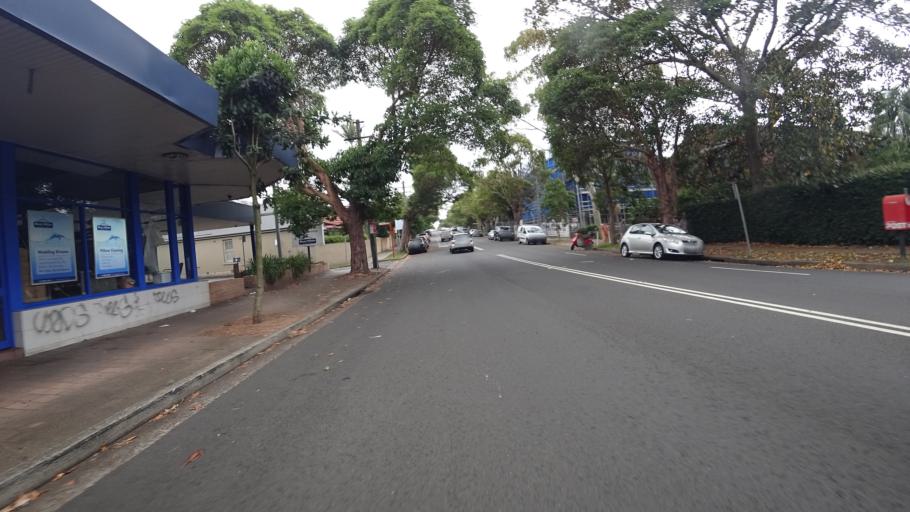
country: AU
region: New South Wales
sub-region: North Sydney
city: Crows Nest
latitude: -33.8283
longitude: 151.2064
